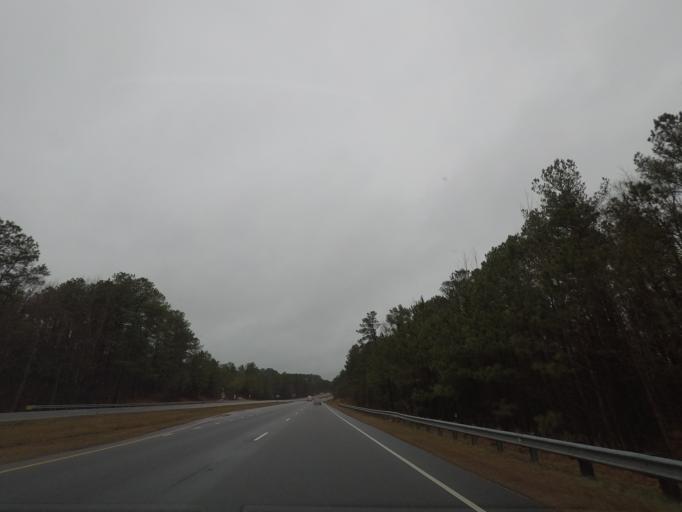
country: US
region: North Carolina
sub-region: Lee County
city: Broadway
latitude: 35.3245
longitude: -79.0924
